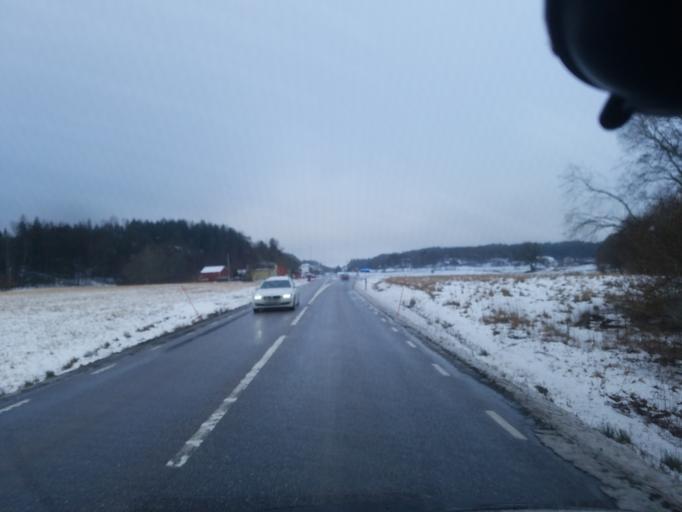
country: SE
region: Vaestra Goetaland
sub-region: Orust
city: Henan
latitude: 58.3307
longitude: 11.6418
